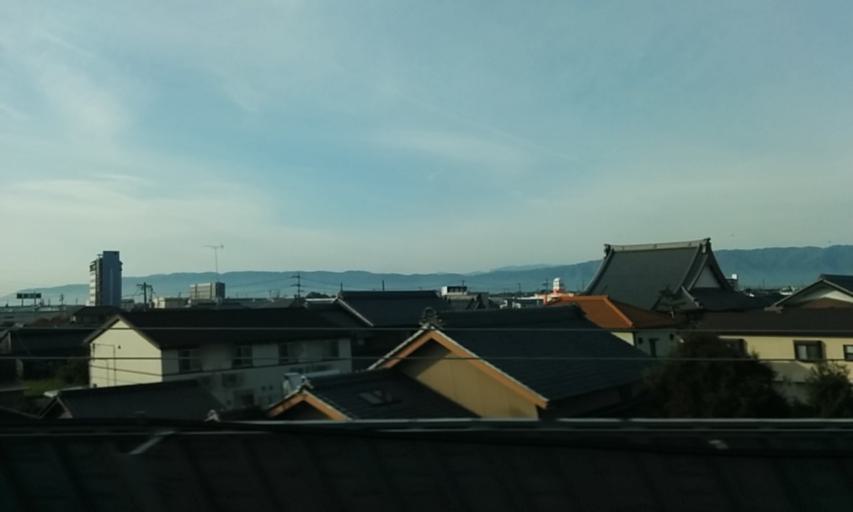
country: JP
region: Aichi
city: Sobue
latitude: 35.3124
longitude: 136.6897
